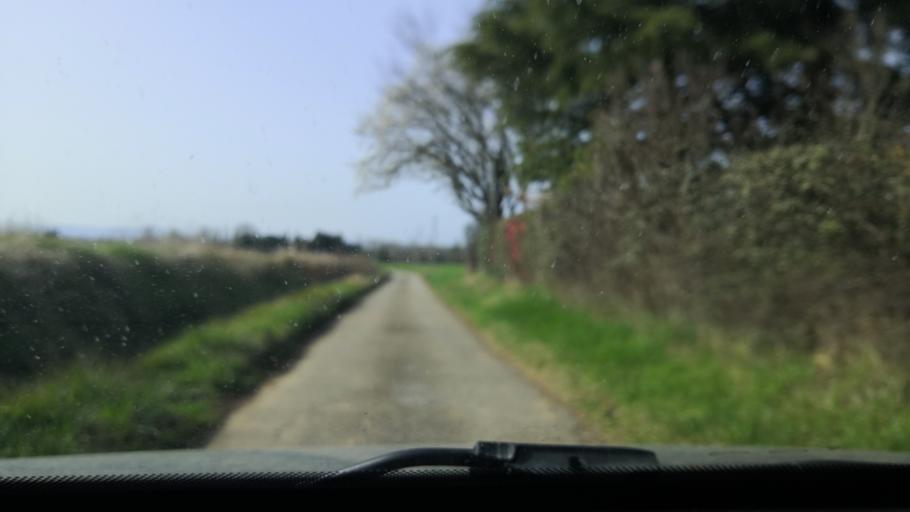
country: FR
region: Rhone-Alpes
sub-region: Departement de la Drome
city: La Begude-de-Mazenc
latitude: 44.5570
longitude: 4.8707
